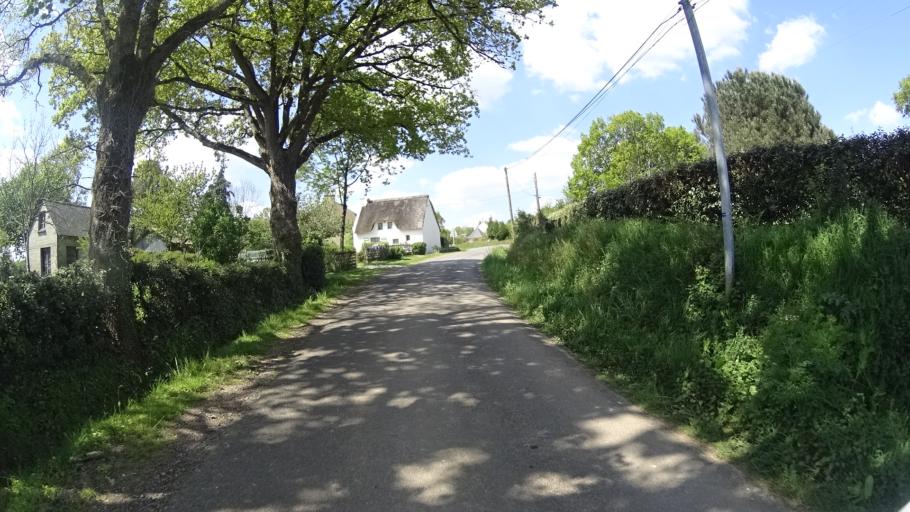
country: FR
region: Brittany
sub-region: Departement du Morbihan
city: Beganne
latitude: 47.5914
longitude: -2.2385
